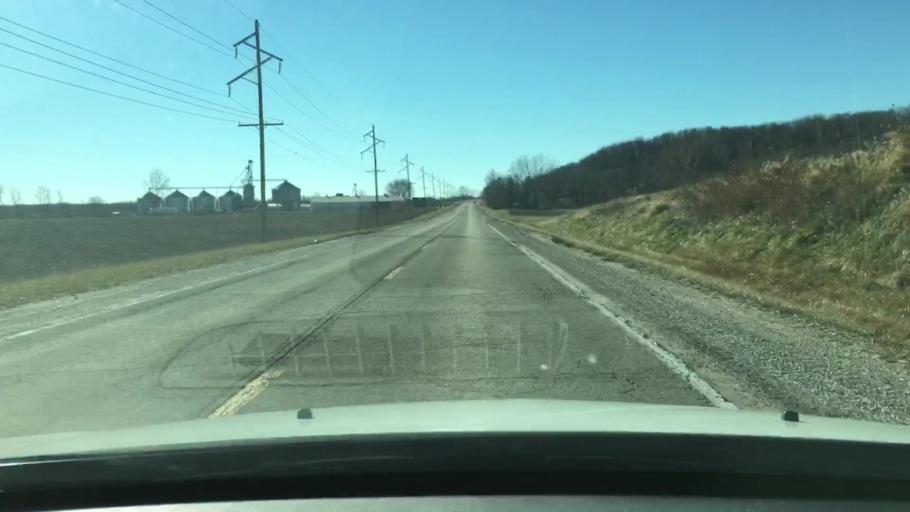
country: US
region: Illinois
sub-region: Fulton County
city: Astoria
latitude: 40.1706
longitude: -90.2903
